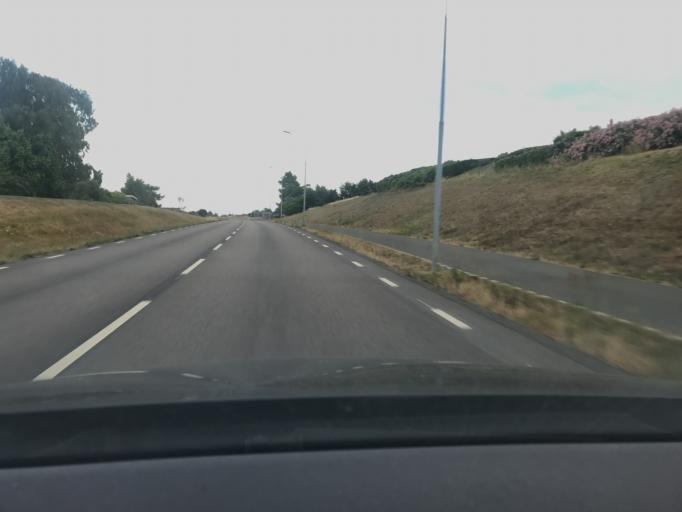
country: SE
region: Skane
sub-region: Simrishamns Kommun
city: Simrishamn
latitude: 55.5486
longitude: 14.3498
